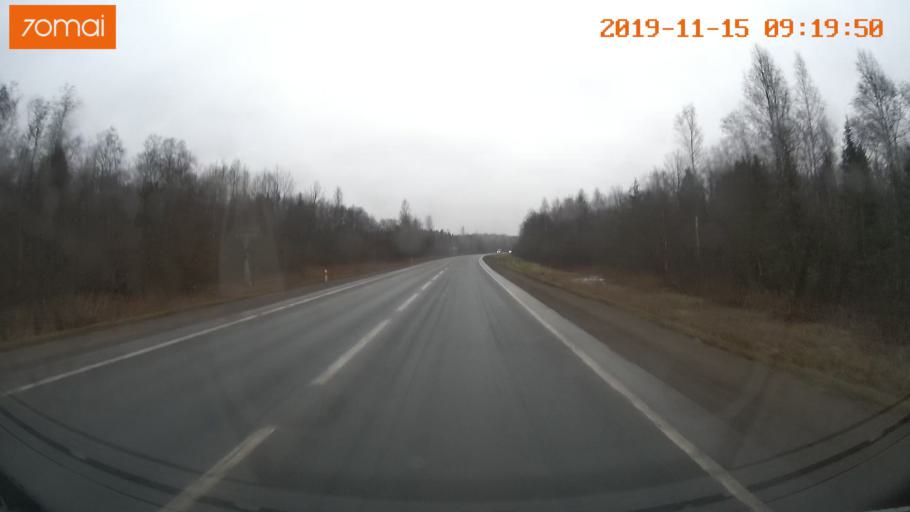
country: RU
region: Vologda
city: Tonshalovo
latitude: 59.2870
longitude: 38.0235
